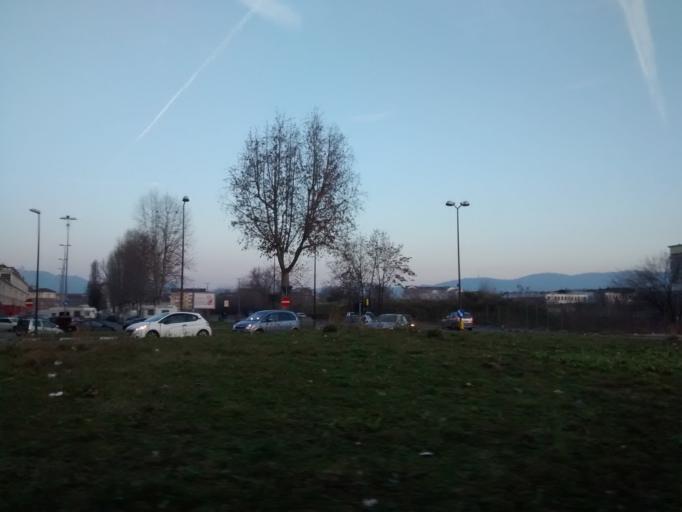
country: IT
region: Piedmont
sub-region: Provincia di Torino
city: Turin
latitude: 45.0909
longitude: 7.6706
